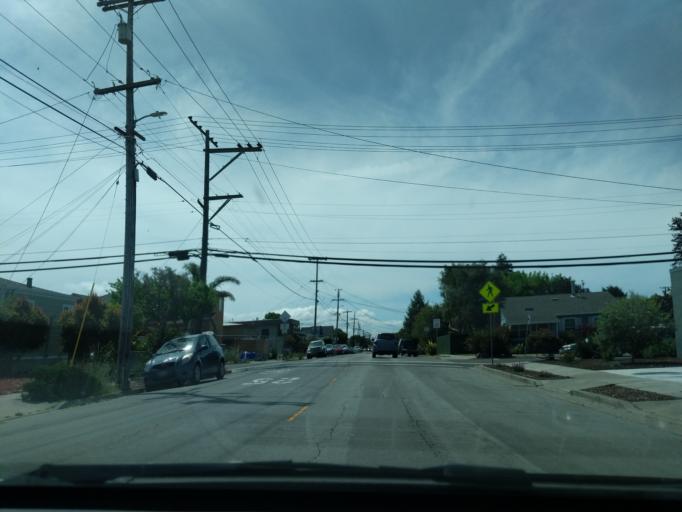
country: US
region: California
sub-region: Contra Costa County
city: El Cerrito
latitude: 37.9209
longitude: -122.3101
